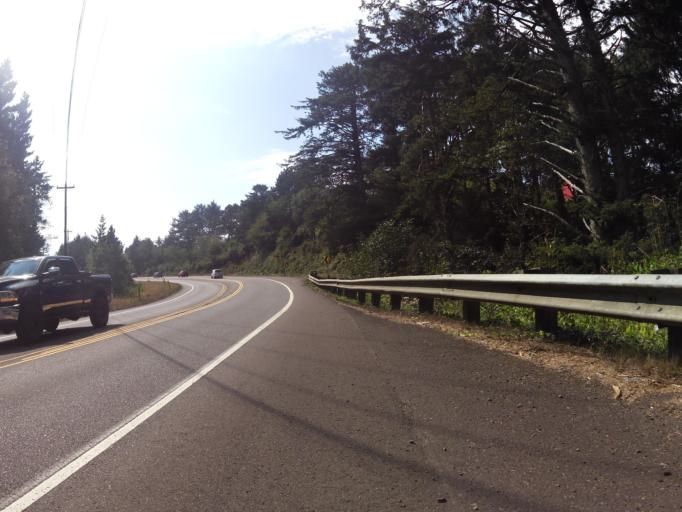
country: US
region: Oregon
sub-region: Lincoln County
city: Waldport
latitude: 44.5199
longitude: -124.0750
